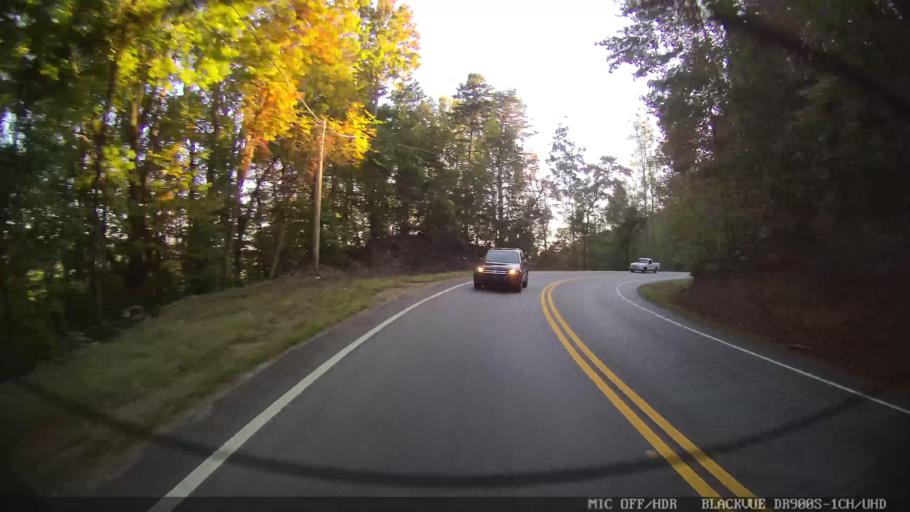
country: US
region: Georgia
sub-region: Lumpkin County
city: Dahlonega
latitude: 34.6158
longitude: -83.9612
